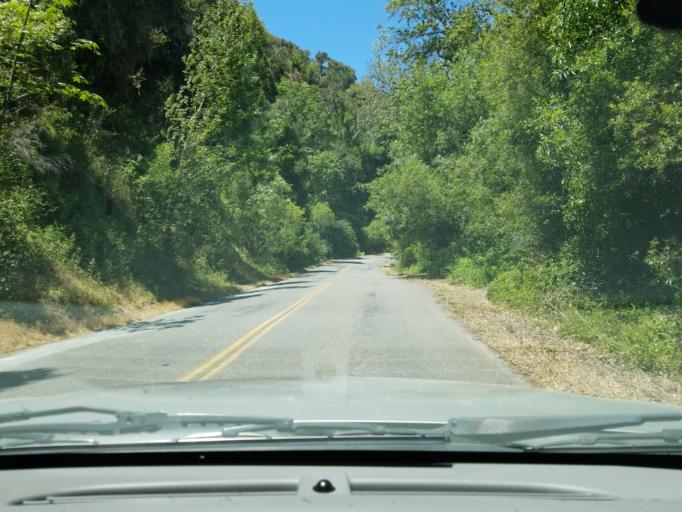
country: US
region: California
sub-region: Monterey County
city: Carmel Valley Village
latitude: 36.4445
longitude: -121.6768
